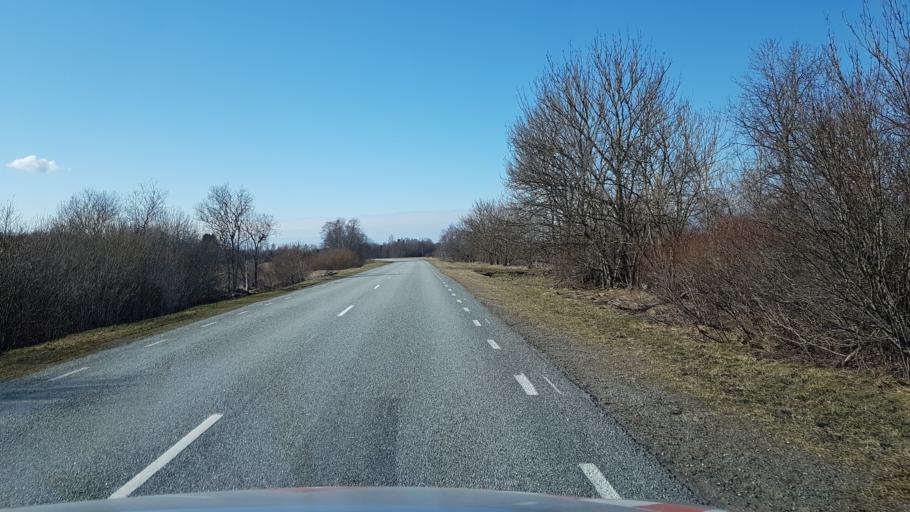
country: EE
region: Laeaene-Virumaa
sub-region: Haljala vald
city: Haljala
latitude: 59.4980
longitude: 26.1362
